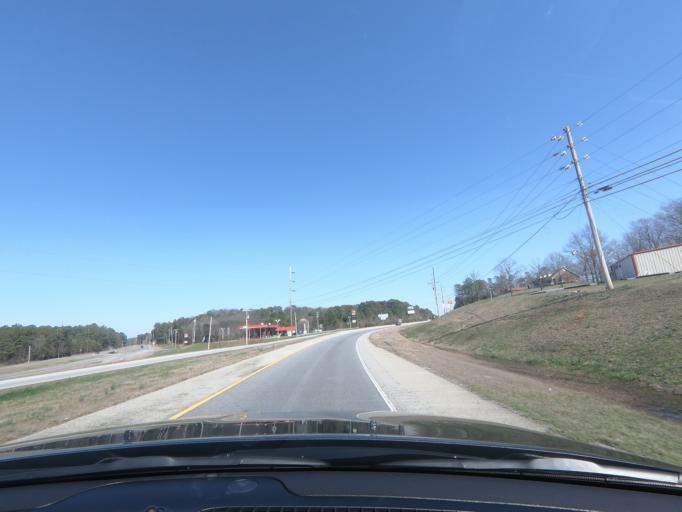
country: US
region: Georgia
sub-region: Gordon County
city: Calhoun
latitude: 34.4700
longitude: -84.9750
